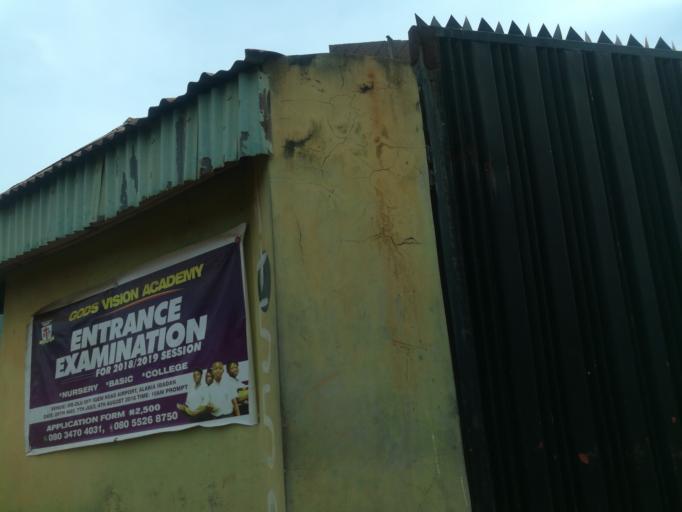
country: NG
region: Oyo
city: Ibadan
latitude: 7.3676
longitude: 3.9701
